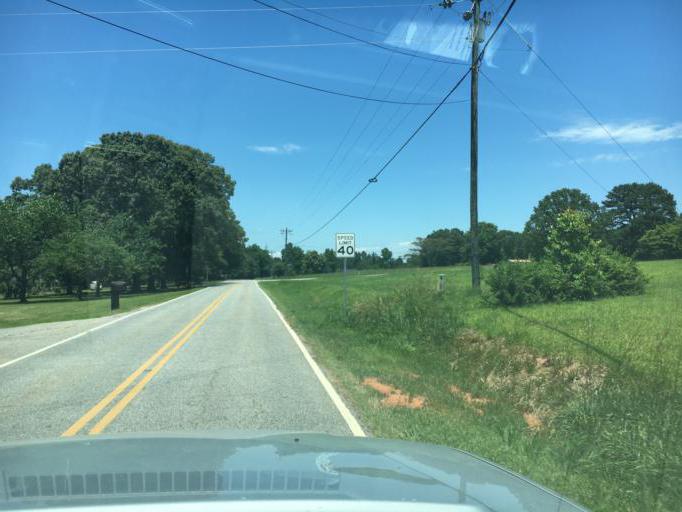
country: US
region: South Carolina
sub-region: Spartanburg County
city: Fairforest
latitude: 34.9855
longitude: -82.0598
